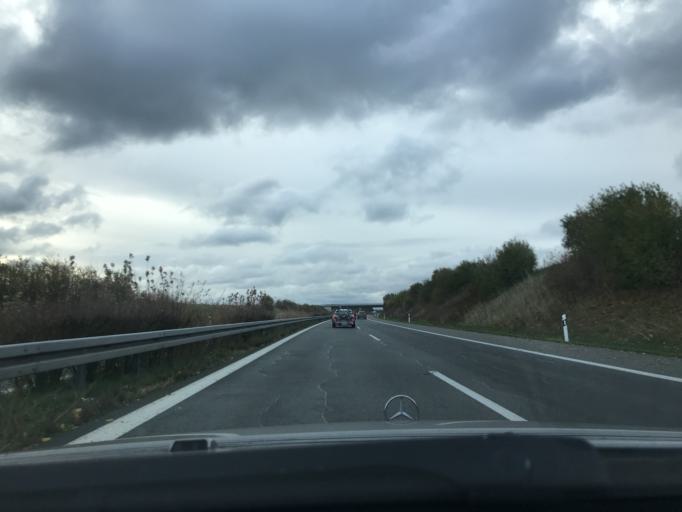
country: DE
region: Mecklenburg-Vorpommern
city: Brunn
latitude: 53.6416
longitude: 13.3699
